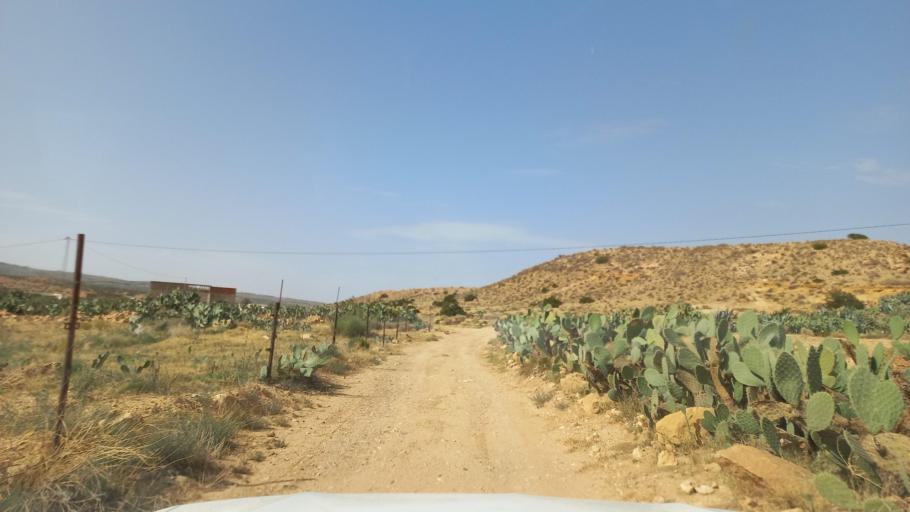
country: TN
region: Al Qasrayn
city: Kasserine
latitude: 35.3064
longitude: 8.9407
